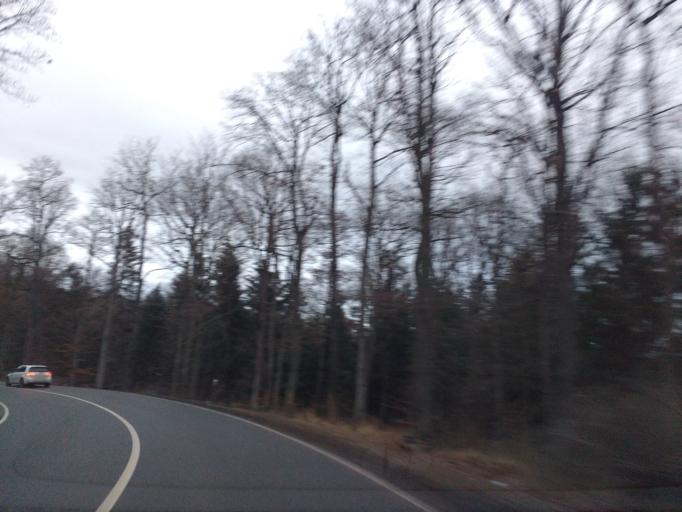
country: DE
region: Saxony-Anhalt
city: Neinstedt
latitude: 51.7109
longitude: 11.0804
